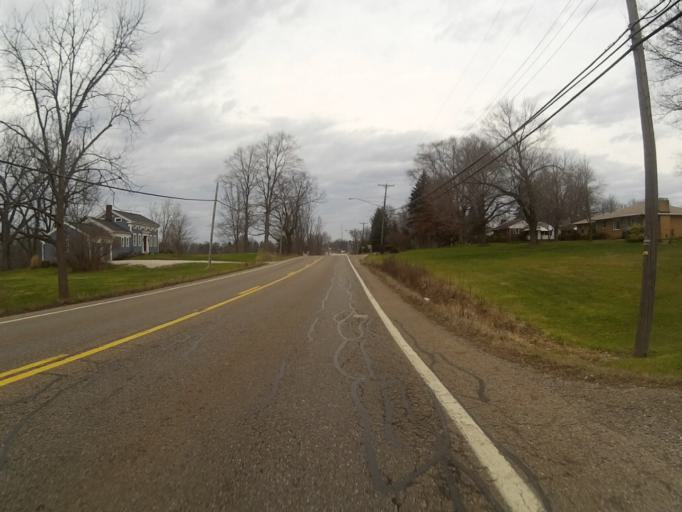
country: US
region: Ohio
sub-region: Portage County
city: Brimfield
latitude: 41.0936
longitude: -81.3464
